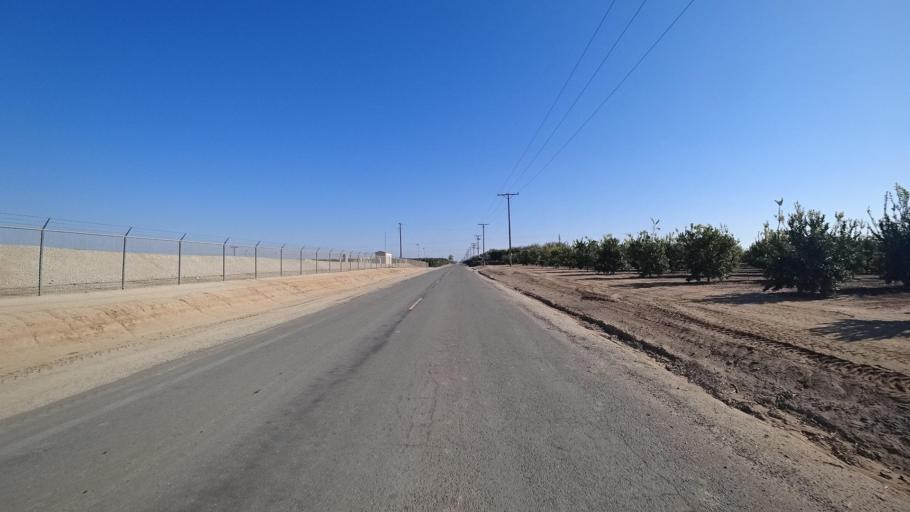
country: US
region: California
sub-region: Tulare County
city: Richgrove
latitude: 35.7180
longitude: -119.1444
